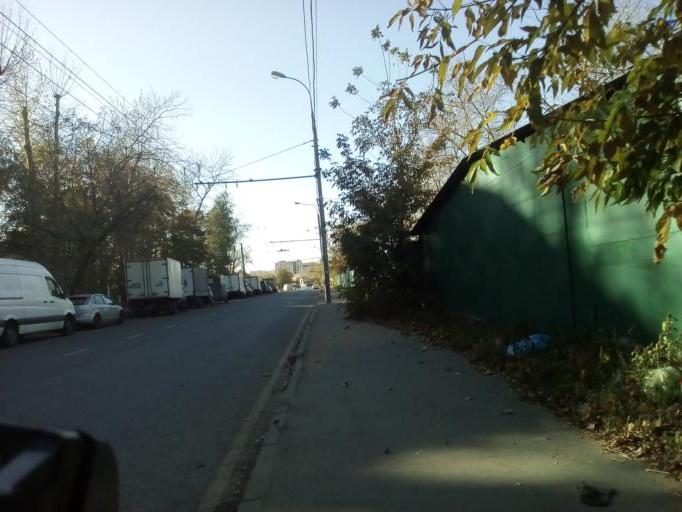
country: RU
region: Moscow
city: Likhobory
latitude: 55.8486
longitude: 37.5713
